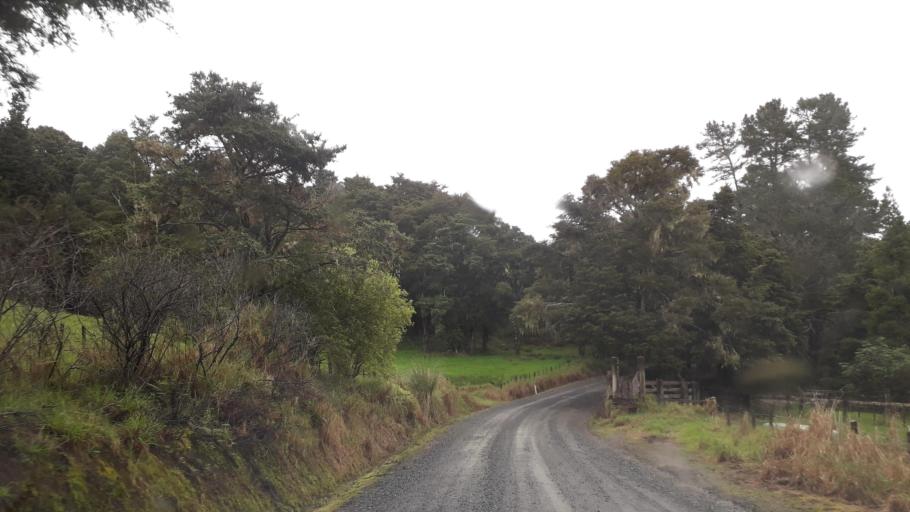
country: NZ
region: Northland
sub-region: Far North District
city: Waimate North
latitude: -35.1336
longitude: 173.7156
